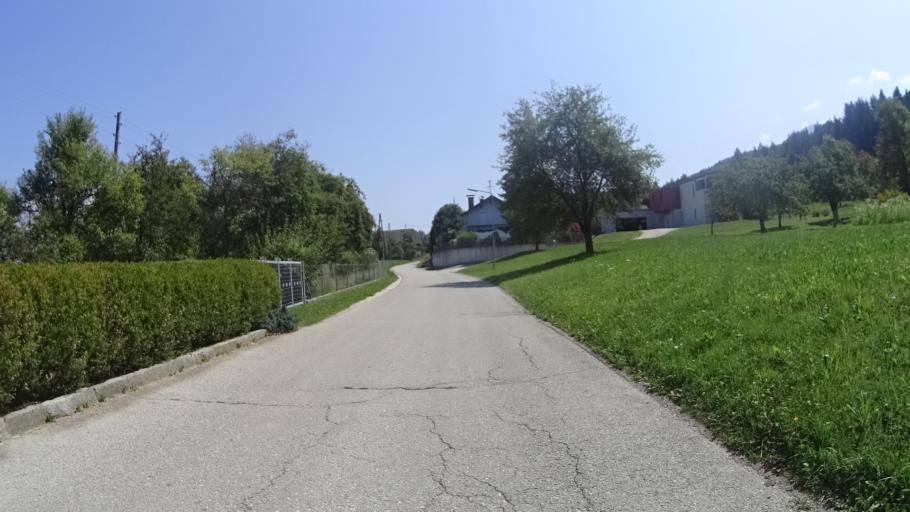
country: AT
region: Carinthia
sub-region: Politischer Bezirk Volkermarkt
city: Globasnitz
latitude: 46.5594
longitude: 14.6718
